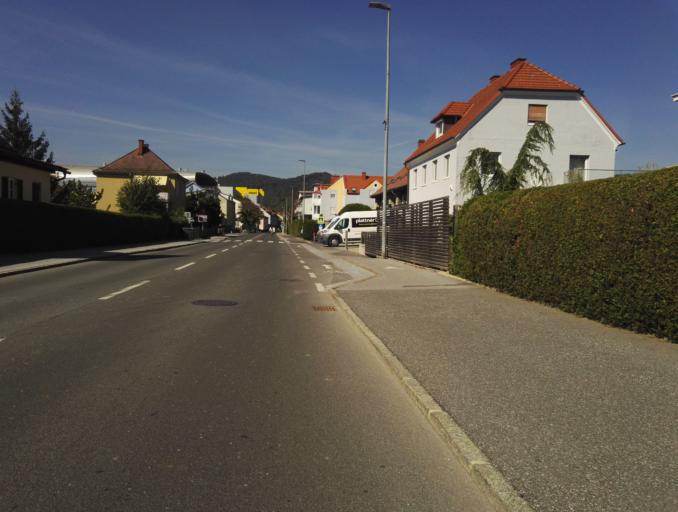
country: AT
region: Styria
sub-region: Politischer Bezirk Graz-Umgebung
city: Gratkorn
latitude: 47.1305
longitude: 15.3421
